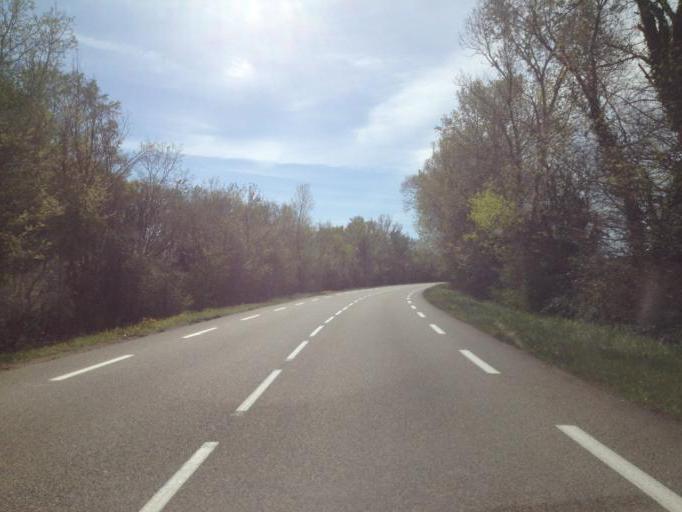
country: FR
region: Provence-Alpes-Cote d'Azur
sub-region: Departement du Vaucluse
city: Caderousse
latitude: 44.1118
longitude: 4.7262
